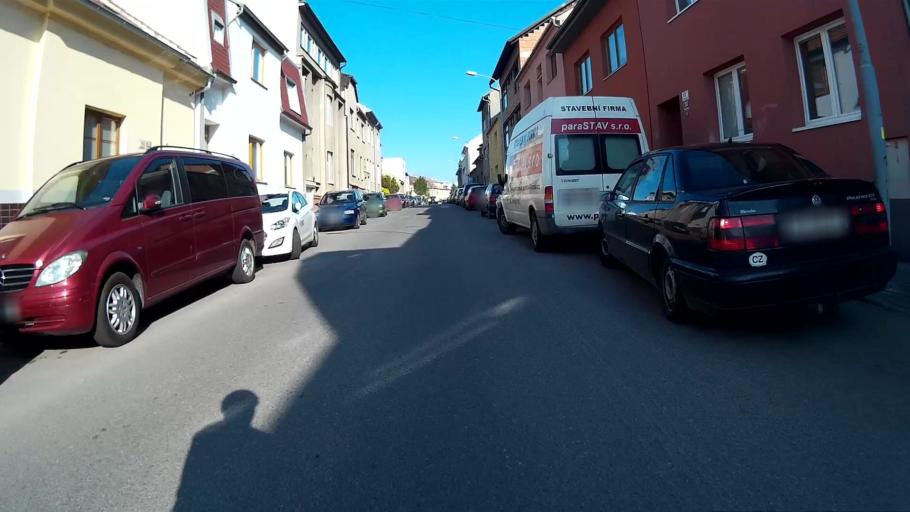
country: CZ
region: South Moravian
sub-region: Mesto Brno
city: Brno
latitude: 49.2095
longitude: 16.5846
